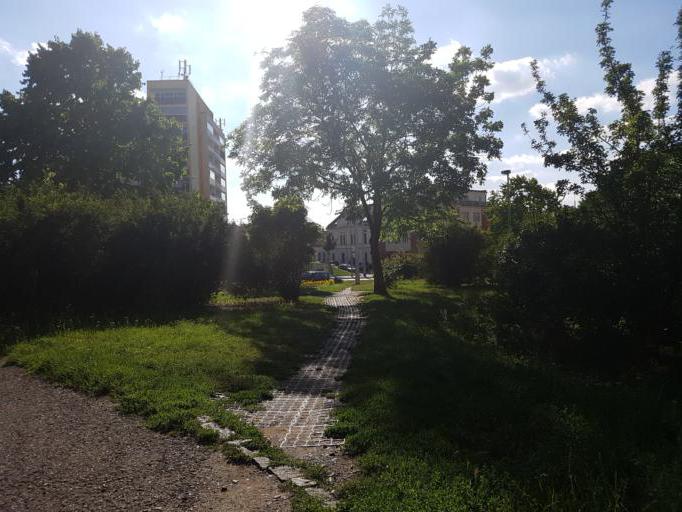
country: CZ
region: Praha
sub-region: Praha 8
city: Liben
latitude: 50.0697
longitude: 14.4907
